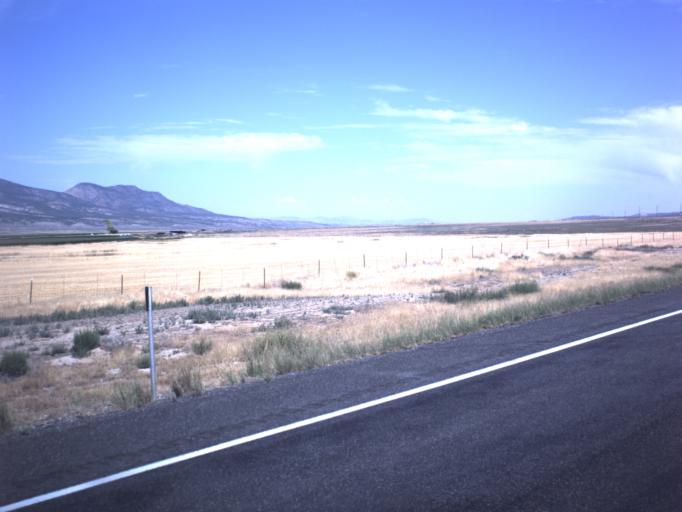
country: US
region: Utah
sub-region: Sanpete County
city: Gunnison
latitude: 39.2327
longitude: -111.8477
